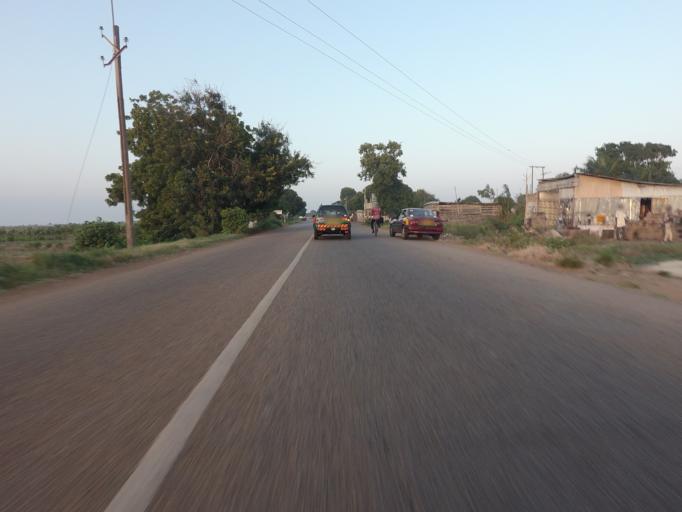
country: GH
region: Volta
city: Anloga
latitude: 5.7993
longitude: 0.9131
